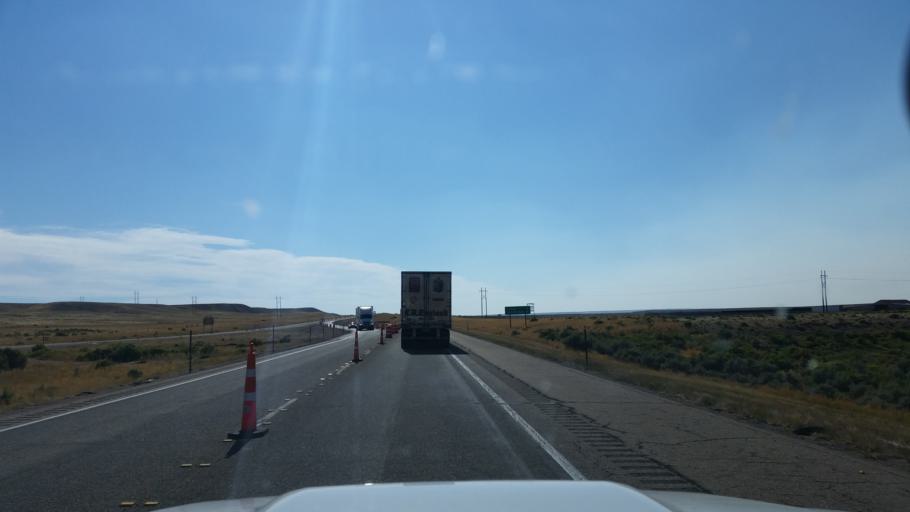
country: US
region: Wyoming
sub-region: Uinta County
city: Lyman
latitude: 41.3883
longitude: -110.2054
